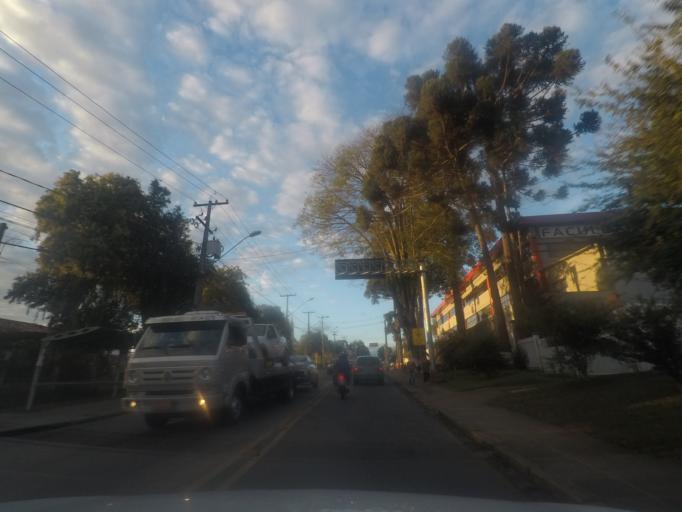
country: BR
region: Parana
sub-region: Pinhais
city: Pinhais
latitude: -25.4452
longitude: -49.1895
